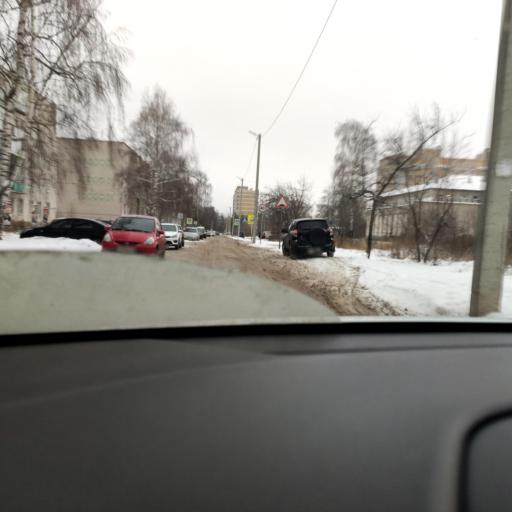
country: RU
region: Tatarstan
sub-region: Zelenodol'skiy Rayon
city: Zelenodolsk
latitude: 55.8559
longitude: 48.4947
